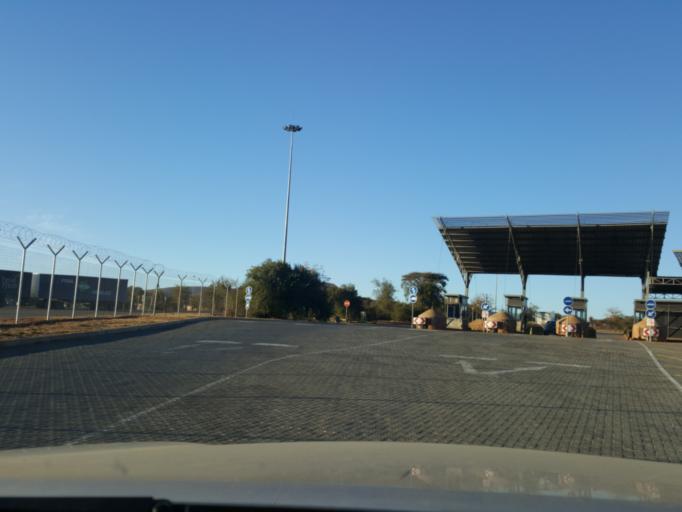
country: BW
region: South East
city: Lobatse
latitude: -25.2759
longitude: 25.7138
